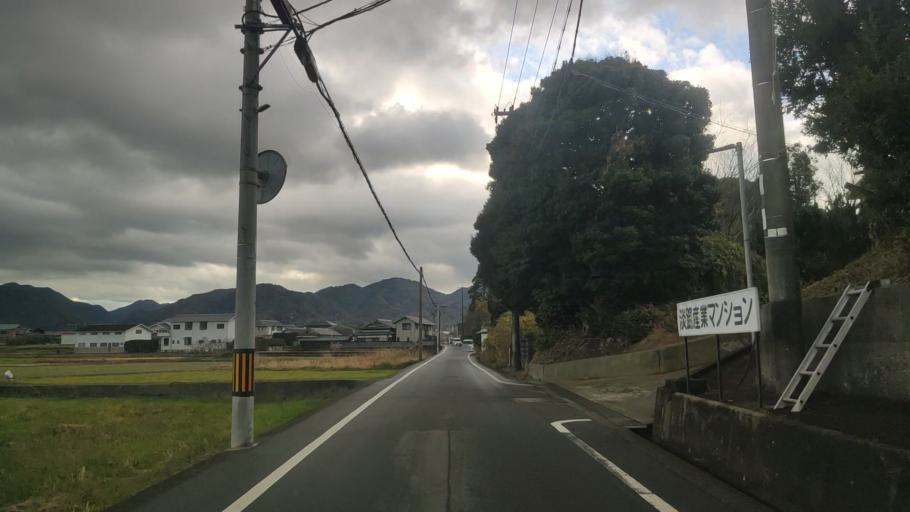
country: JP
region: Hyogo
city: Sumoto
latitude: 34.3292
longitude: 134.8533
